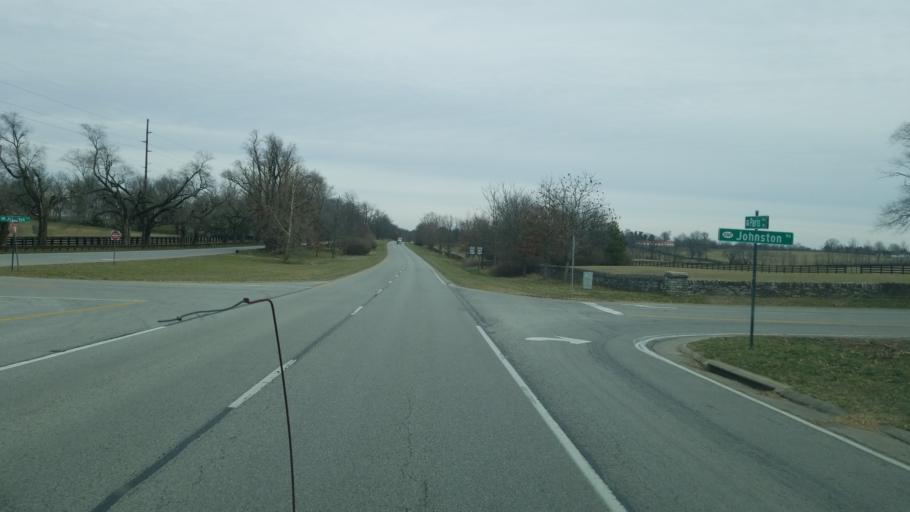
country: US
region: Kentucky
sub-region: Fayette County
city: Lexington-Fayette
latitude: 38.0982
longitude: -84.4205
